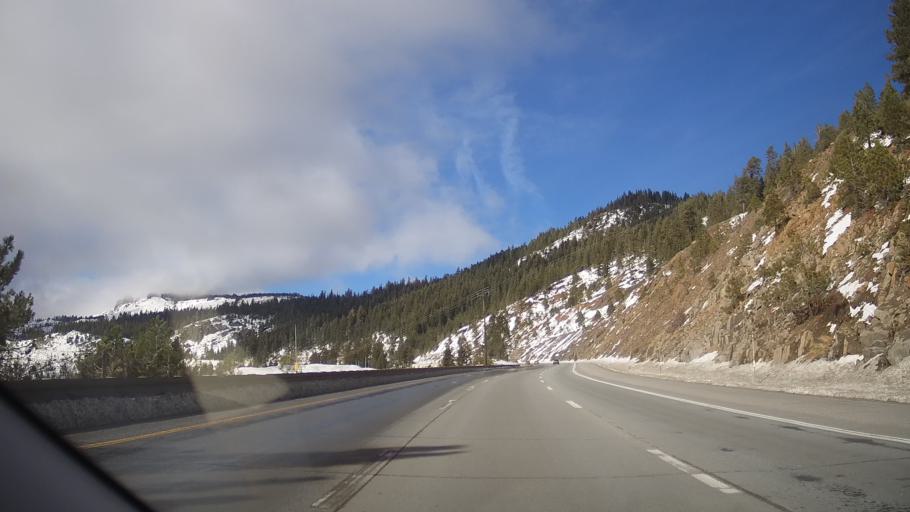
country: US
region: California
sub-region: Nevada County
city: Truckee
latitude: 39.3344
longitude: -120.3051
